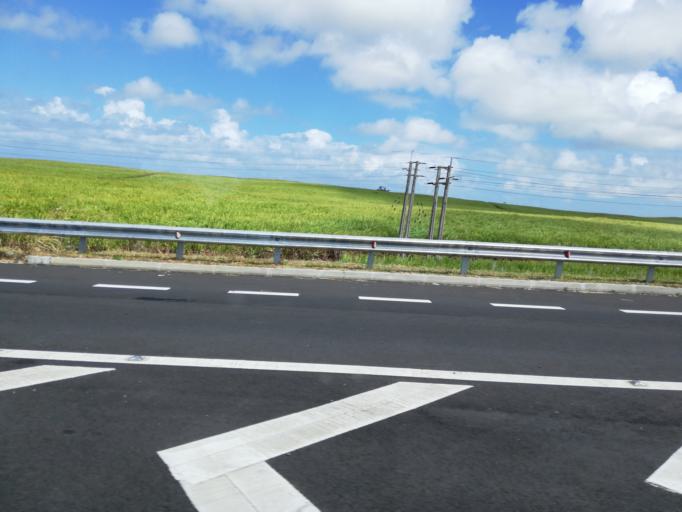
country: MU
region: Grand Port
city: Plaine Magnien
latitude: -20.4329
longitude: 57.6451
